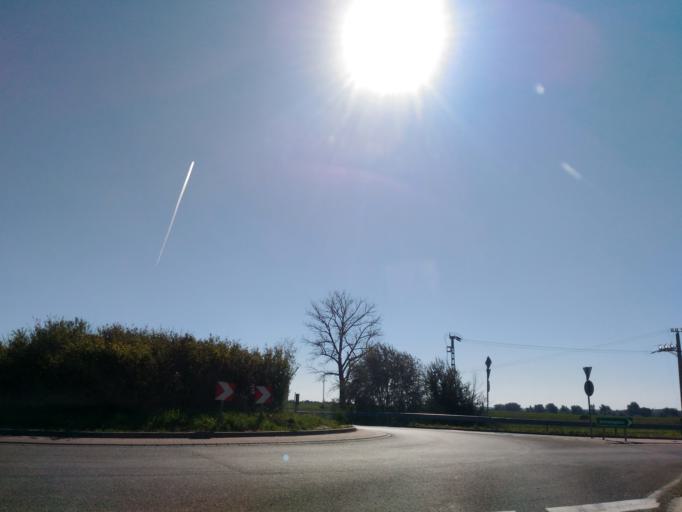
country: HU
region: Fejer
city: Ivancsa
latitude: 47.1293
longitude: 18.8157
